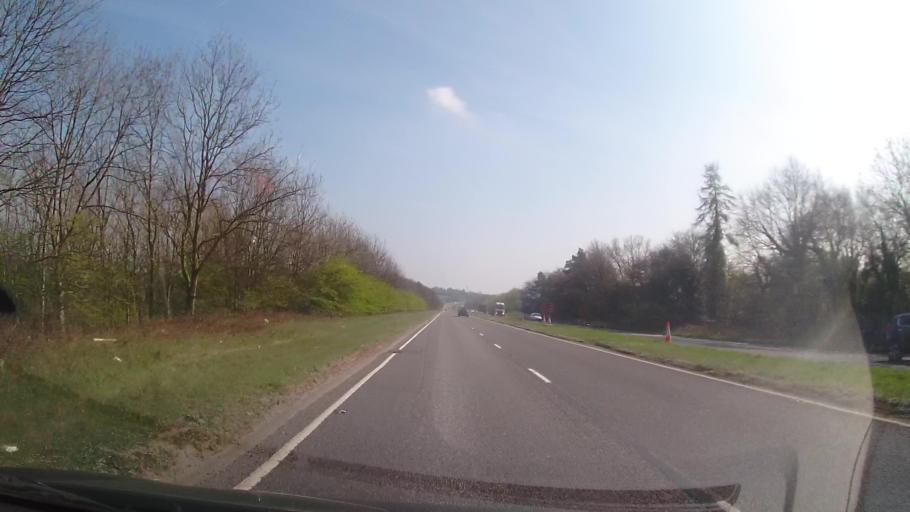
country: GB
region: England
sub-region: Leicestershire
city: Markfield
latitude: 52.6921
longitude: -1.2769
